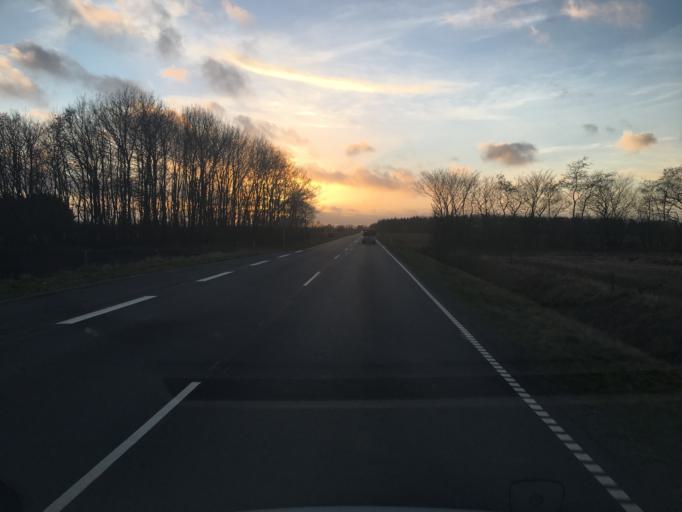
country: DE
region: Schleswig-Holstein
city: Boxlund
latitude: 54.9325
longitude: 9.1397
